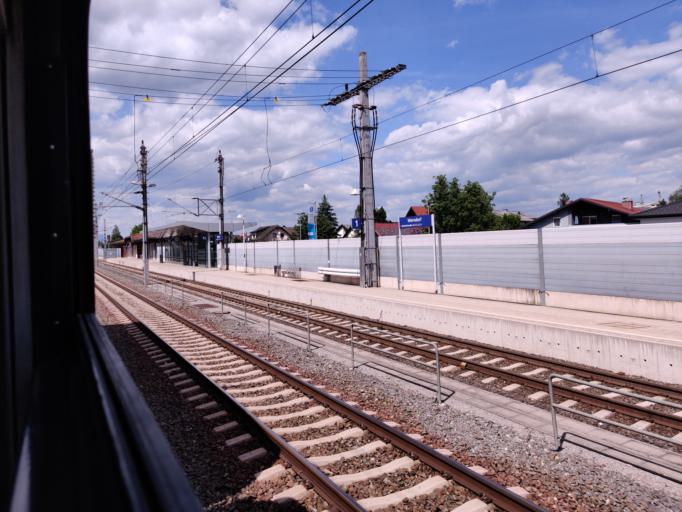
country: AT
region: Styria
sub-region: Politischer Bezirk Graz-Umgebung
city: Werndorf
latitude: 46.9156
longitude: 15.4770
